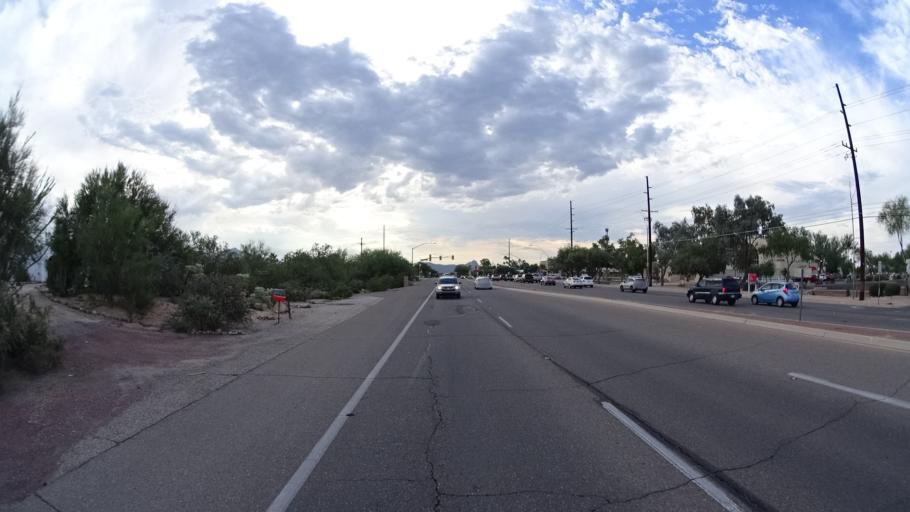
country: US
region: Arizona
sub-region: Pima County
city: Casas Adobes
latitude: 32.3369
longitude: -111.0113
